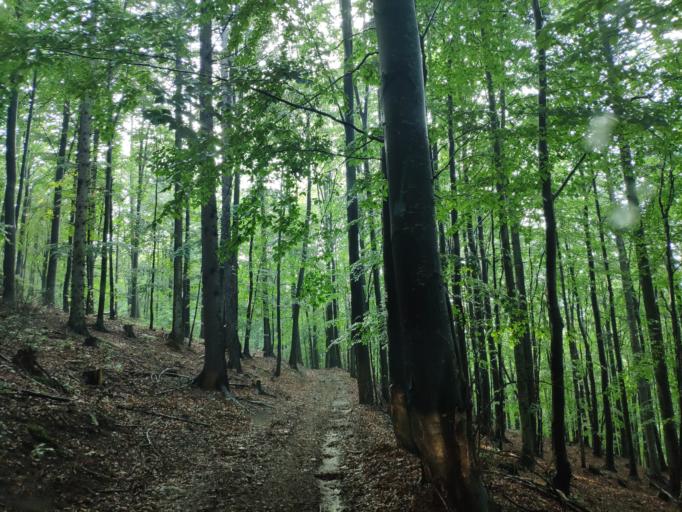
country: SK
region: Kosicky
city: Medzev
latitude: 48.7490
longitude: 20.9964
